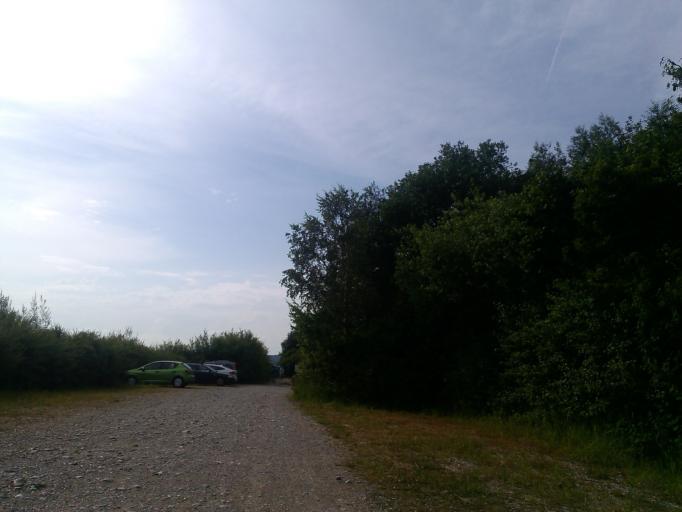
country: DE
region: Bavaria
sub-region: Upper Bavaria
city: Gilching
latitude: 48.1131
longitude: 11.2768
